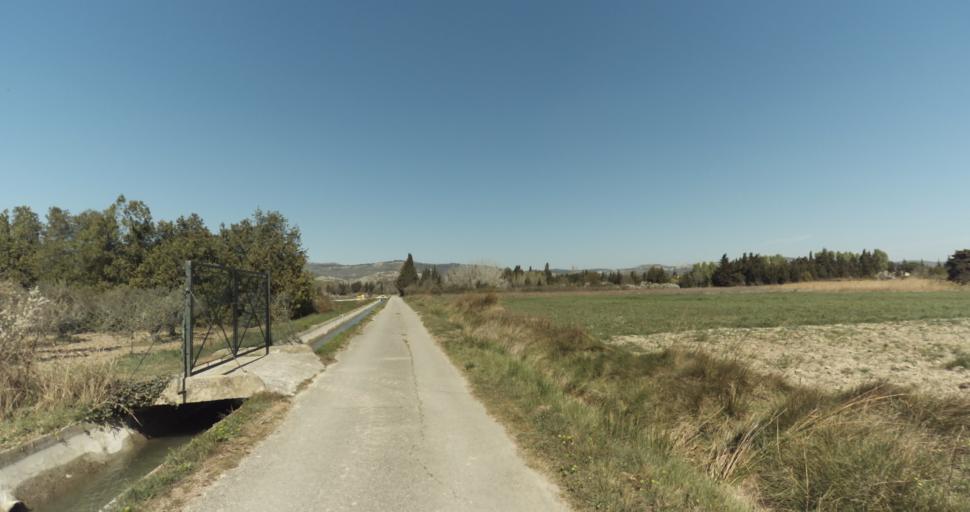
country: FR
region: Provence-Alpes-Cote d'Azur
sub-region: Departement des Bouches-du-Rhone
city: Pelissanne
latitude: 43.6245
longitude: 5.1462
